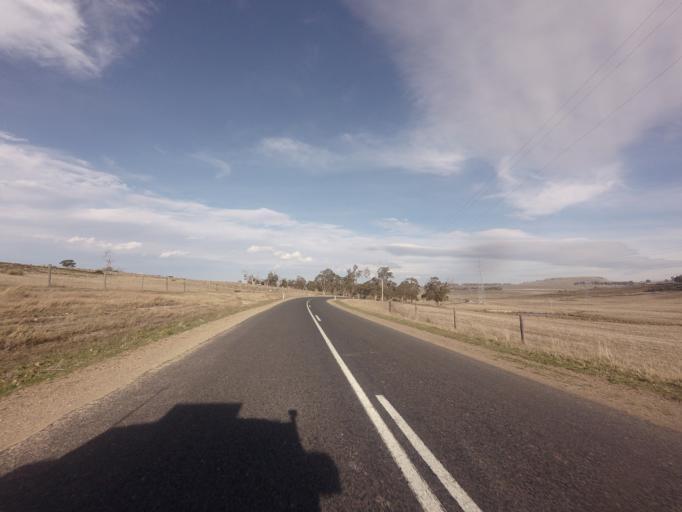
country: AU
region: Tasmania
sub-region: Derwent Valley
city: New Norfolk
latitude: -42.2576
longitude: 146.9369
